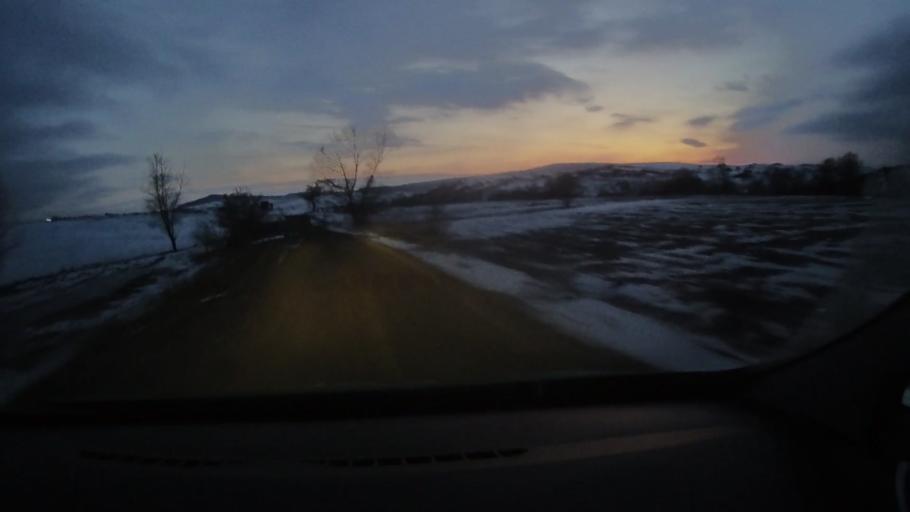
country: RO
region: Harghita
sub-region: Comuna Darjiu
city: Darjiu
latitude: 46.1609
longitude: 25.2074
